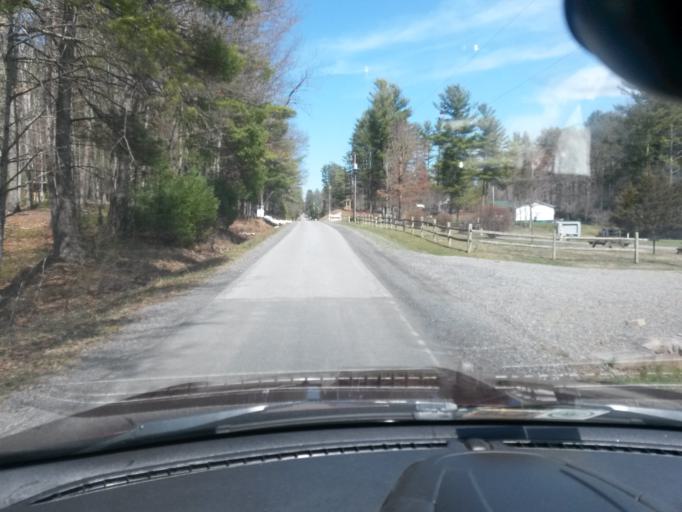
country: US
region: West Virginia
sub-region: Greenbrier County
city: Ronceverte
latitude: 37.6260
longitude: -80.3489
